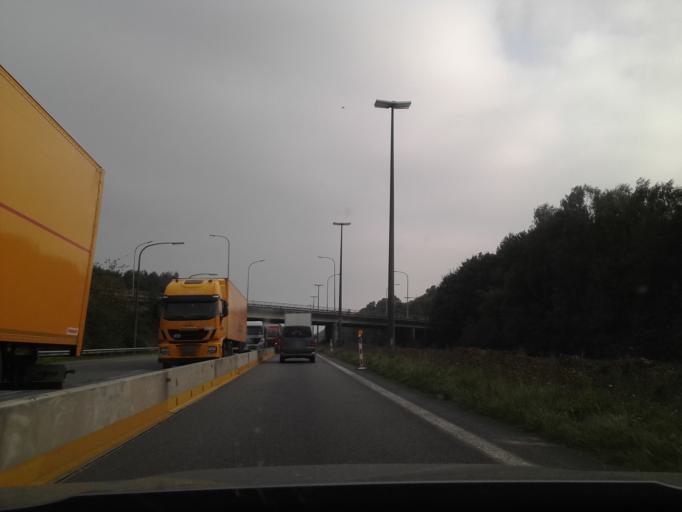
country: FR
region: Nord-Pas-de-Calais
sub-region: Departement du Nord
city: Camphin-en-Pevele
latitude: 50.6089
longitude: 3.2986
